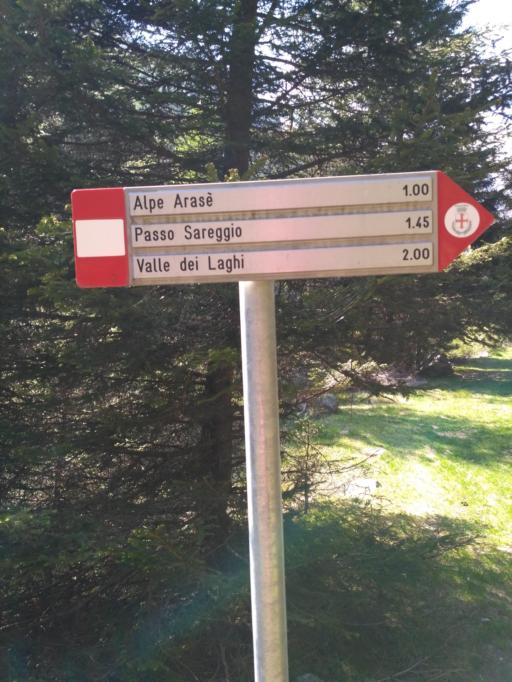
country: CH
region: Grisons
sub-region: Bernina District
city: Poschiavo
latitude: 46.2550
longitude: 10.0278
